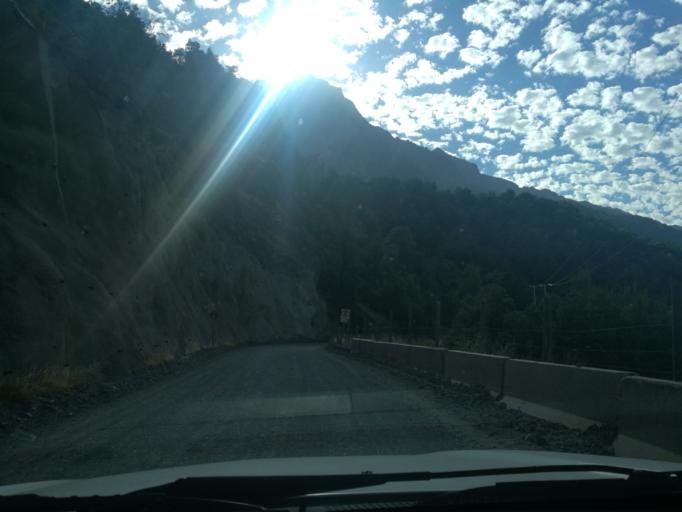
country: CL
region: O'Higgins
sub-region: Provincia de Cachapoal
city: Machali
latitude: -34.2767
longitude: -70.4495
